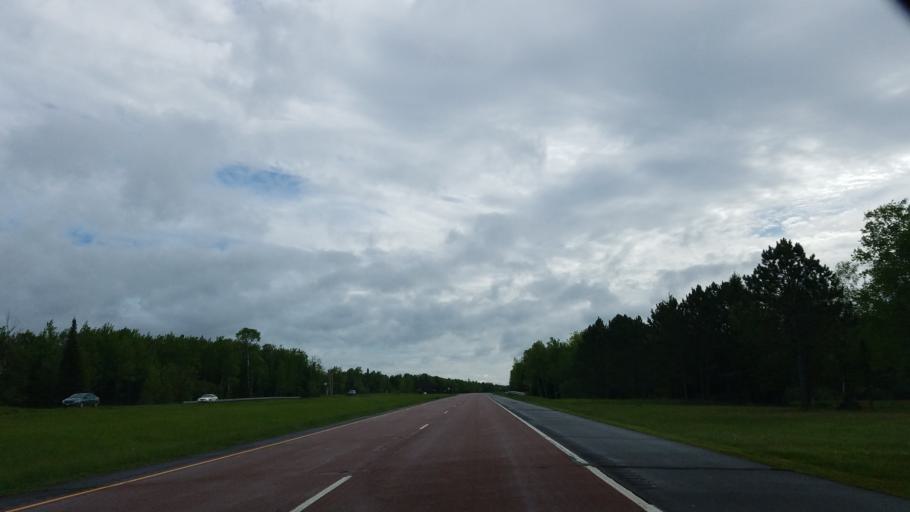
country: US
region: Minnesota
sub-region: Saint Louis County
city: Arnold
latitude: 46.8830
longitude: -91.9333
